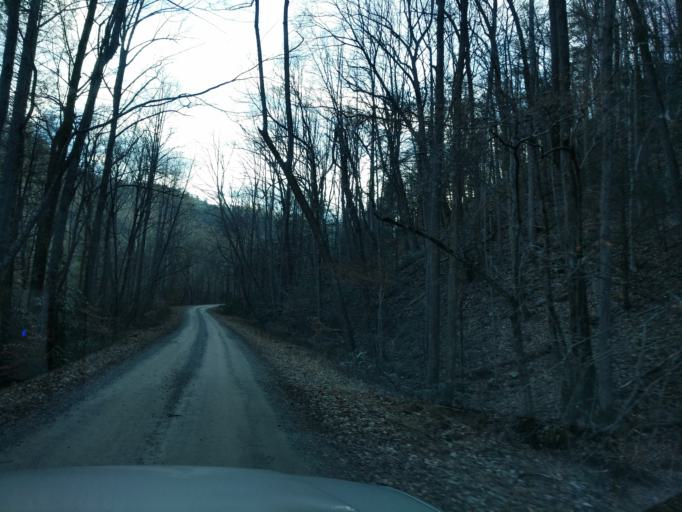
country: US
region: North Carolina
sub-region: Haywood County
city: Cove Creek
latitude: 35.7279
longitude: -83.0249
